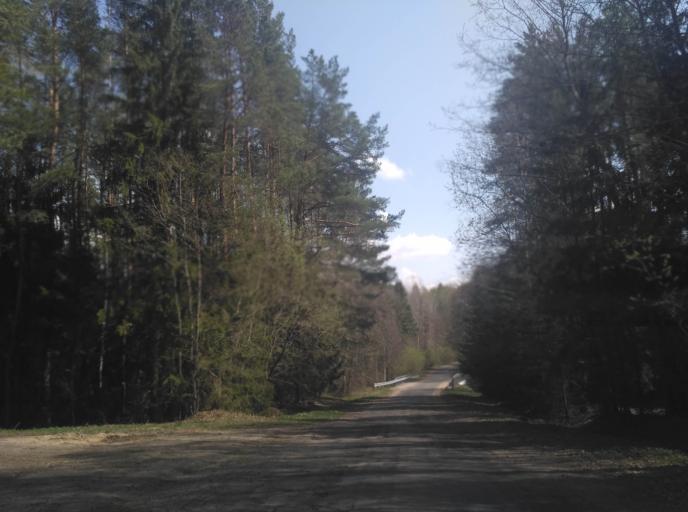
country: BY
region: Minsk
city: Loshnitsa
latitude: 54.4942
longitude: 28.7108
